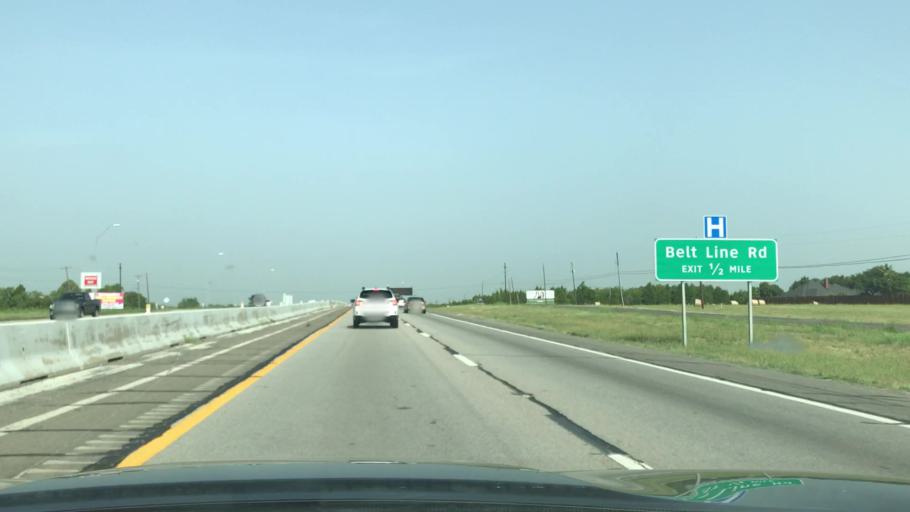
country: US
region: Texas
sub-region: Dallas County
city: Sunnyvale
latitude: 32.7874
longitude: -96.5766
